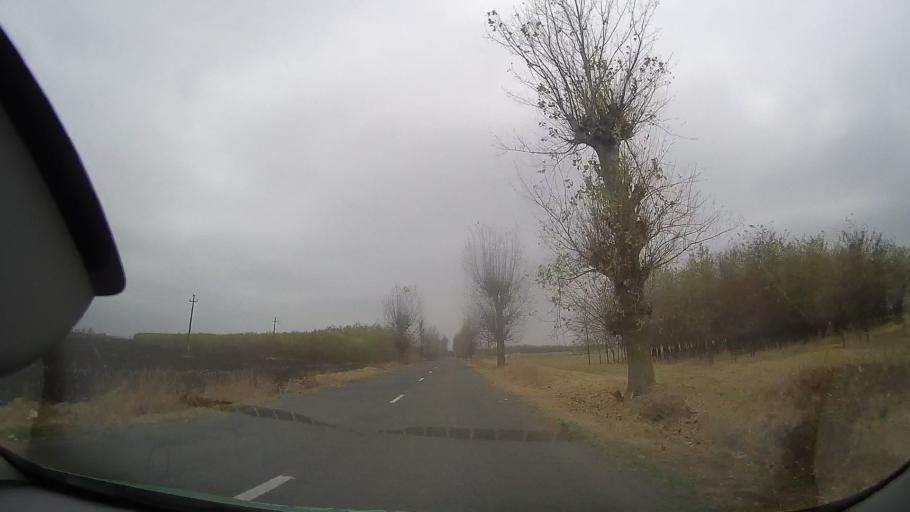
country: RO
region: Ialomita
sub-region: Comuna Grindu
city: Grindu
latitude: 44.7856
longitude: 26.9034
